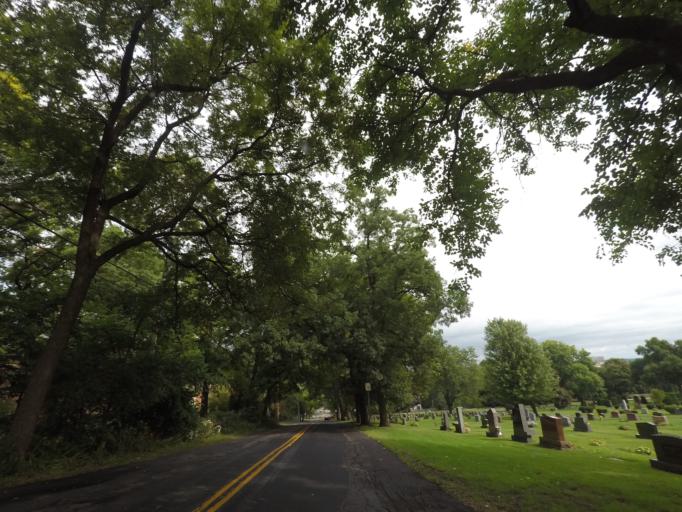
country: US
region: Wisconsin
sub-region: Dane County
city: Shorewood Hills
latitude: 43.0665
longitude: -89.4363
